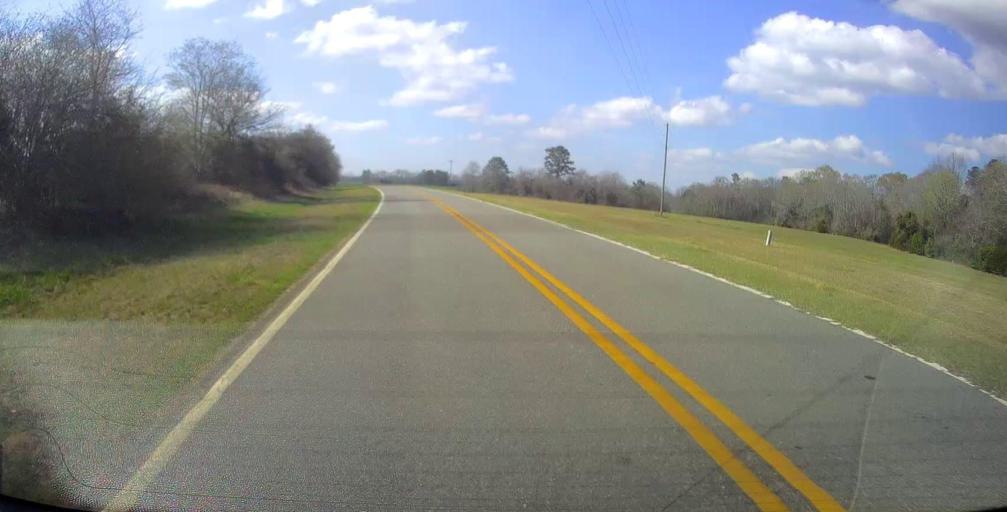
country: US
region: Georgia
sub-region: Wilkinson County
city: Irwinton
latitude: 32.6263
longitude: -83.0936
